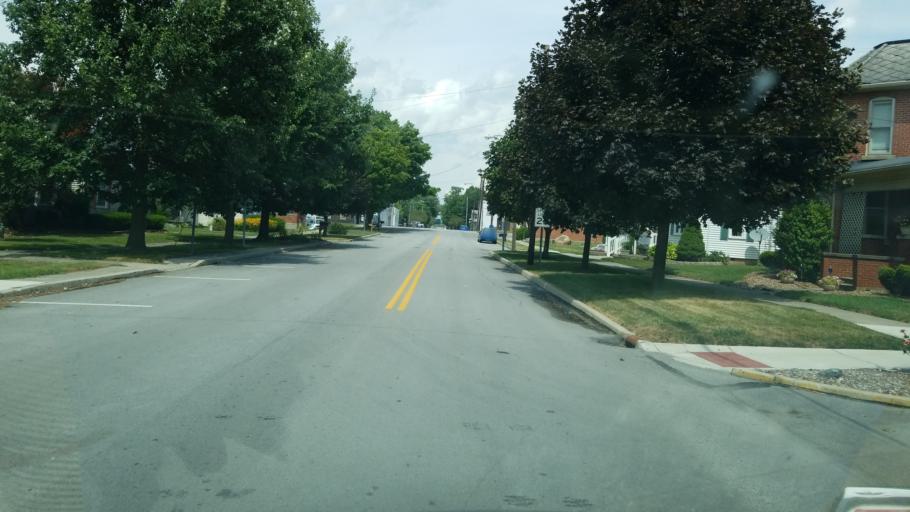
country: US
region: Ohio
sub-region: Hancock County
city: Arlington
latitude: 40.8980
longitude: -83.7271
